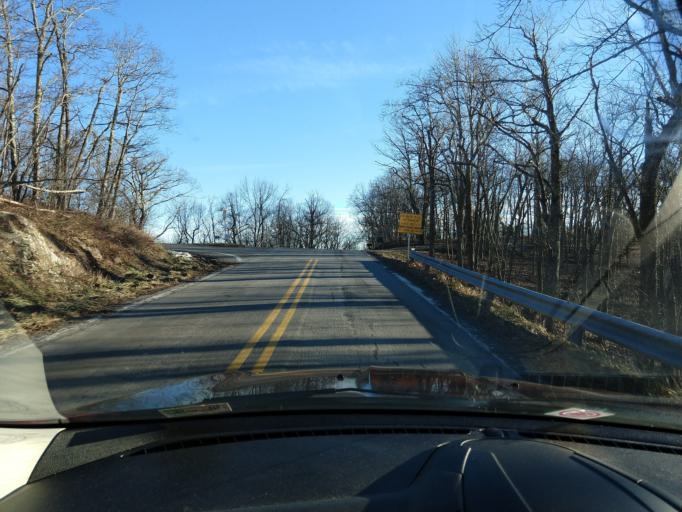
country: US
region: Virginia
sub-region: Alleghany County
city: Clifton Forge
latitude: 37.8750
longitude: -79.8875
